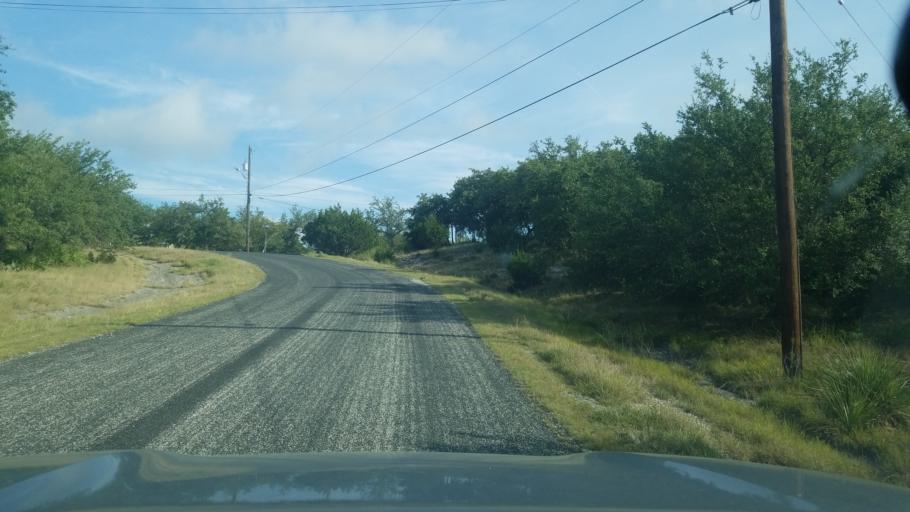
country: US
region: Texas
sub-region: Bexar County
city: Timberwood Park
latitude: 29.6853
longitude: -98.5046
